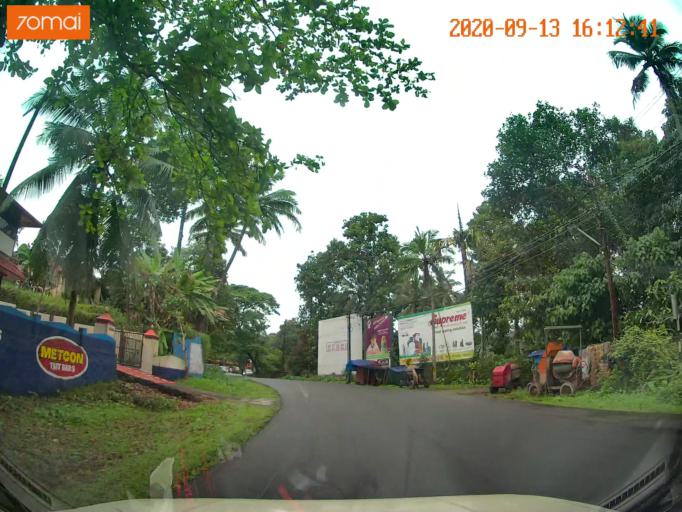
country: IN
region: Kerala
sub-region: Kottayam
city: Palackattumala
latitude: 9.6881
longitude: 76.6208
